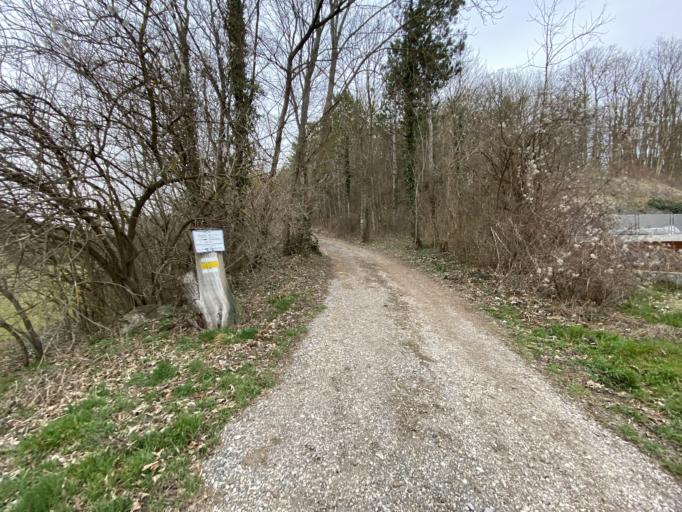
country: AT
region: Lower Austria
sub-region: Politischer Bezirk Modling
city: Gaaden
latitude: 48.0313
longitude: 16.1786
